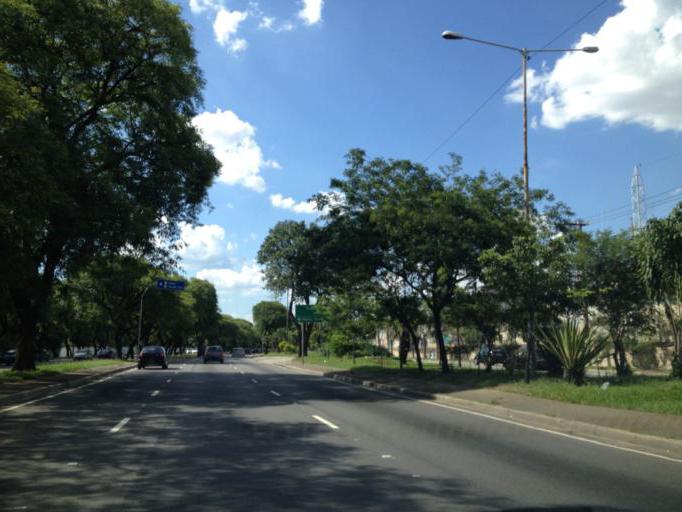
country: BR
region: Sao Paulo
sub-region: Sao Paulo
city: Sao Paulo
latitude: -23.5507
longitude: -46.5781
